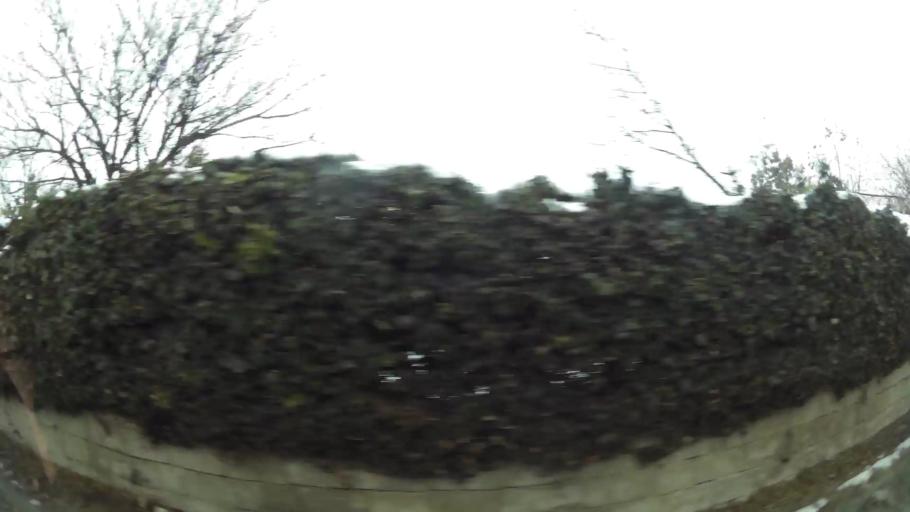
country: MK
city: Kondovo
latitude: 42.0410
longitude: 21.3474
